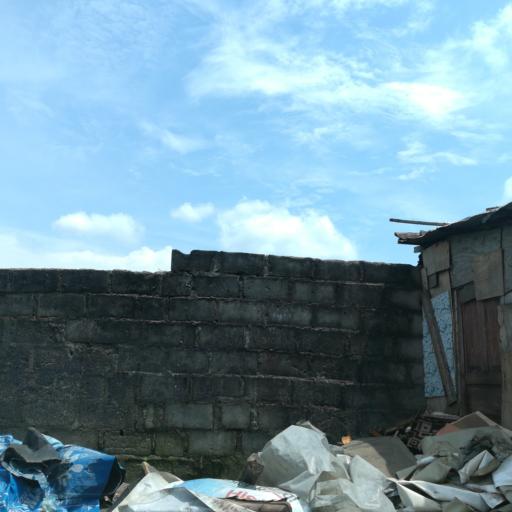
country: NG
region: Rivers
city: Port Harcourt
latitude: 4.7812
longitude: 7.0401
